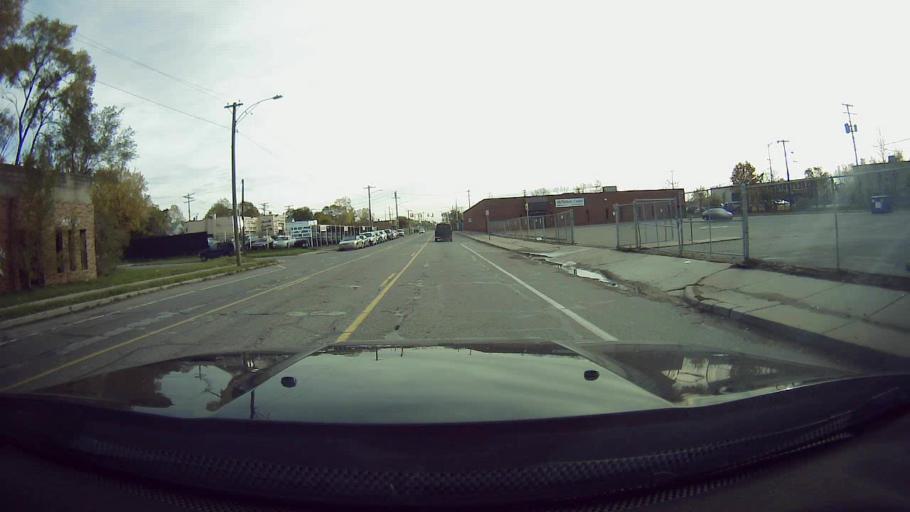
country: US
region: Michigan
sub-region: Wayne County
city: Highland Park
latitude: 42.4185
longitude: -83.0797
